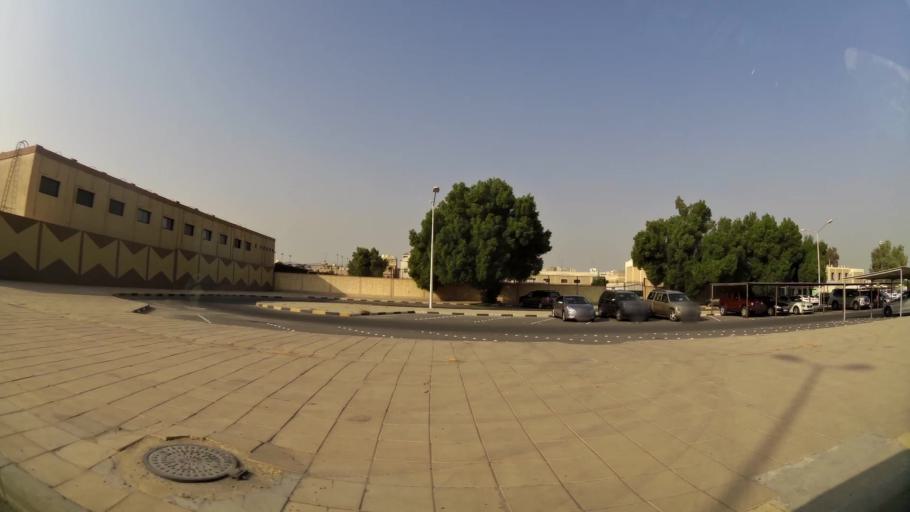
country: KW
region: Muhafazat Hawalli
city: Salwa
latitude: 29.2842
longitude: 48.0684
